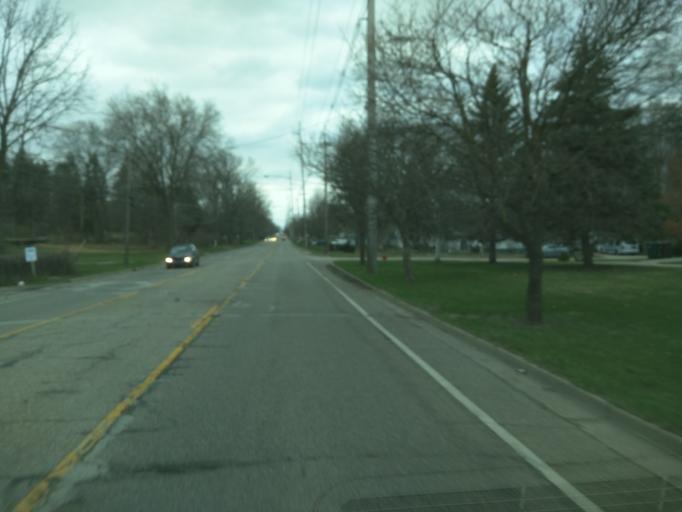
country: US
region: Michigan
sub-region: Ingham County
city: Lansing
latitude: 42.7040
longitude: -84.5234
